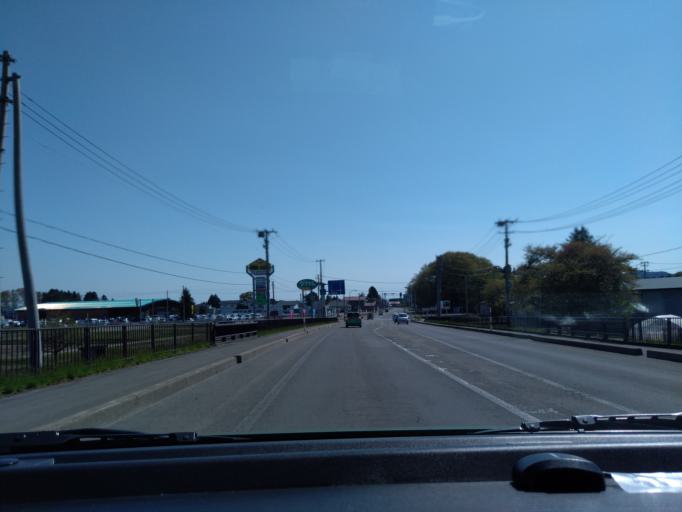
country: JP
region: Akita
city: Kakunodatemachi
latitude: 39.5774
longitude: 140.5662
